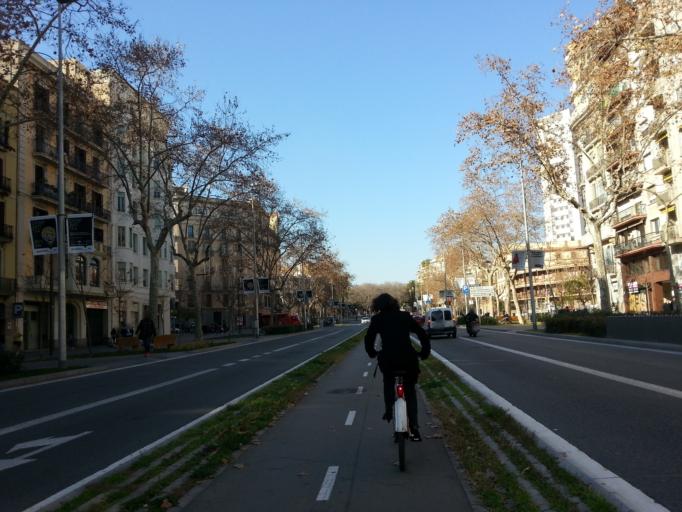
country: ES
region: Catalonia
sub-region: Provincia de Barcelona
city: Ciutat Vella
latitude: 41.3933
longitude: 2.1776
